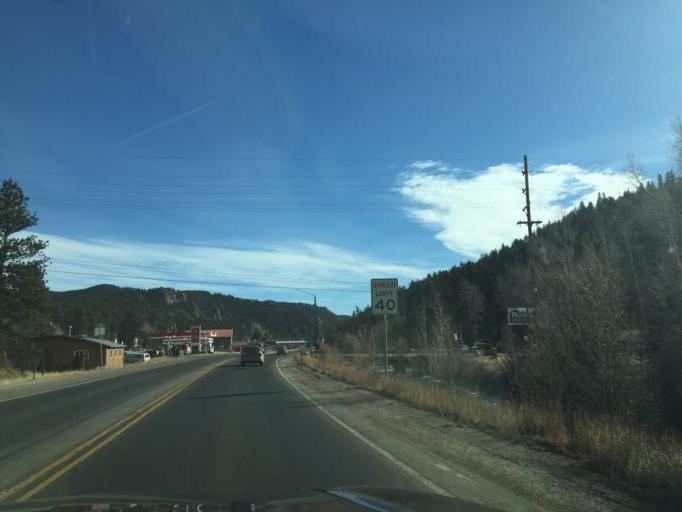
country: US
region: Colorado
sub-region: Jefferson County
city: Evergreen
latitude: 39.4066
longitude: -105.4792
